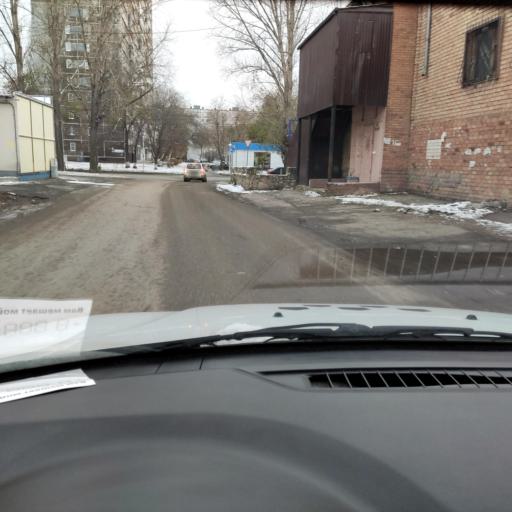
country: RU
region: Samara
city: Tol'yatti
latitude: 53.5392
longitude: 49.2710
